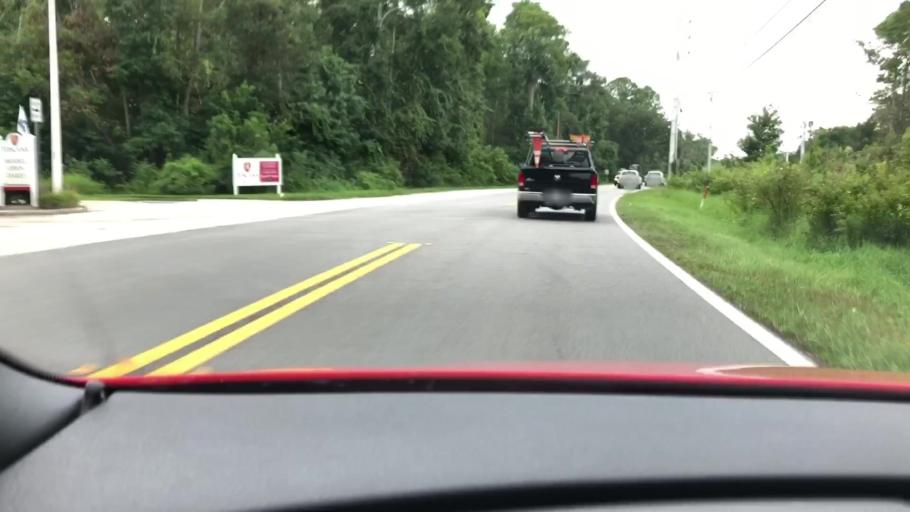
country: US
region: Florida
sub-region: Flagler County
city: Flagler Beach
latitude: 29.5058
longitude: -81.1910
